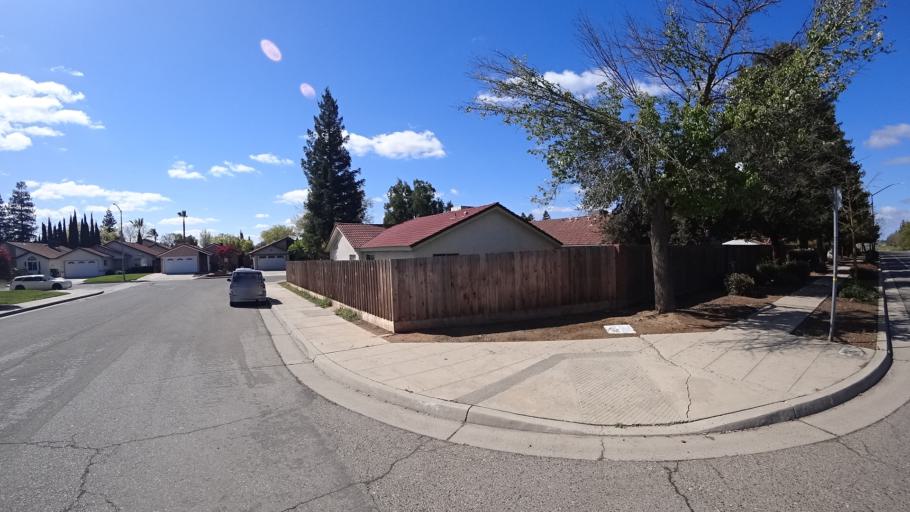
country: US
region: California
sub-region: Fresno County
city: Biola
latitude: 36.8297
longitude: -119.8940
